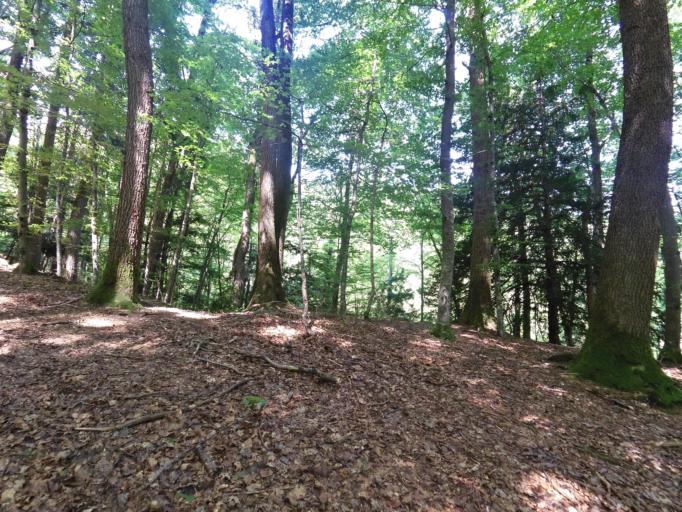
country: CH
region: Thurgau
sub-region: Frauenfeld District
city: Thundorf
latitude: 47.5701
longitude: 8.9888
